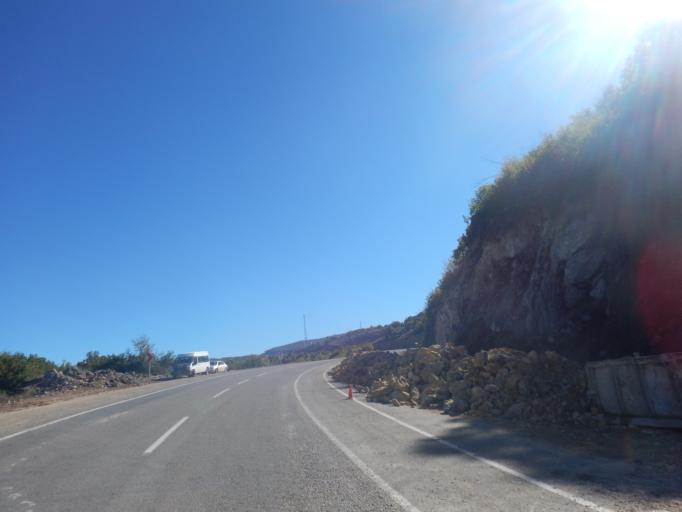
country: TR
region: Ordu
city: Mesudiye
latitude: 40.4557
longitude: 37.7738
